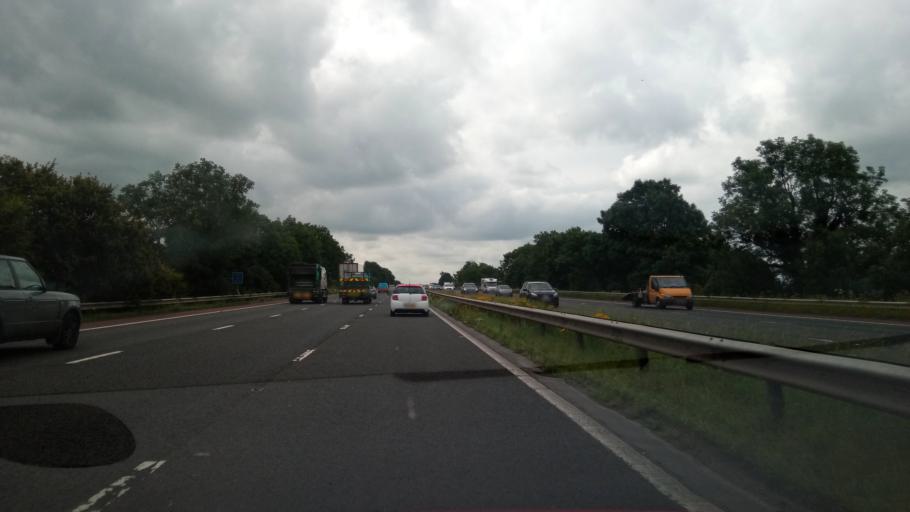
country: GB
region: England
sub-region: Lancashire
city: Galgate
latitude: 53.9994
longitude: -2.7804
